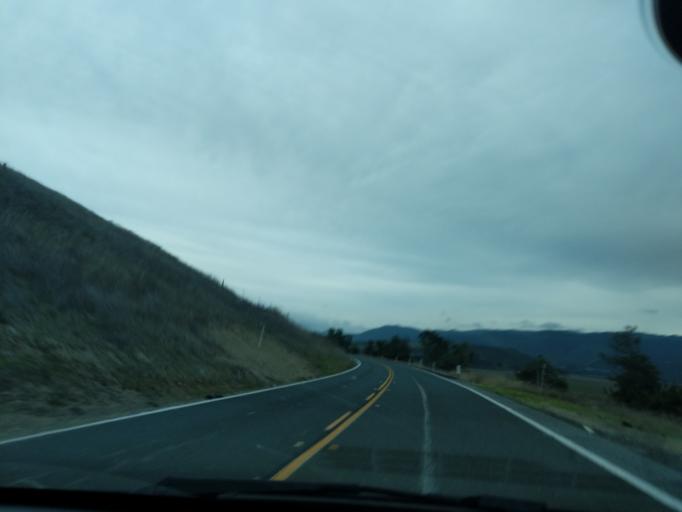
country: US
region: California
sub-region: San Benito County
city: Ridgemark
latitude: 36.7033
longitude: -121.2755
